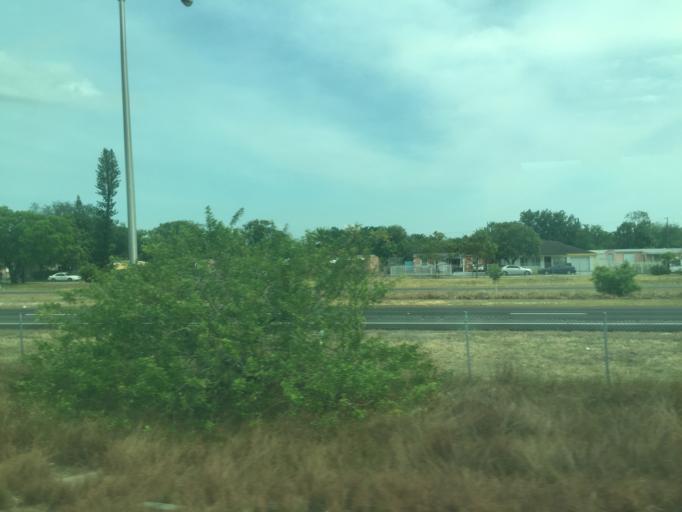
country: US
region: Florida
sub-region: Miami-Dade County
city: Opa-locka
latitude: 25.9063
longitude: -80.2400
